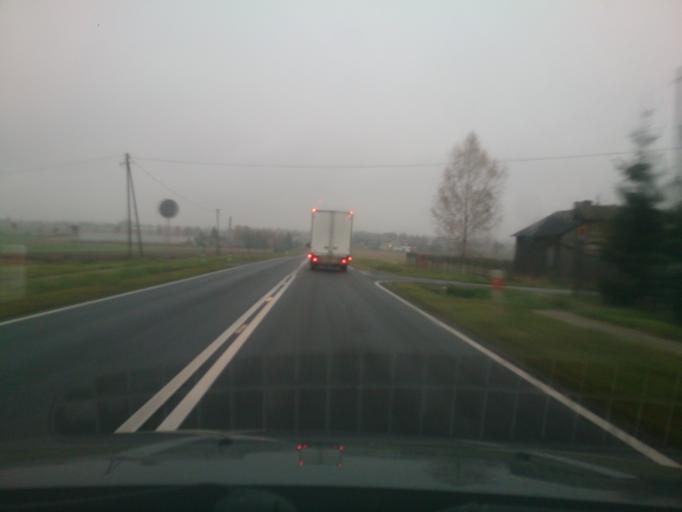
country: PL
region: Greater Poland Voivodeship
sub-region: Powiat kaliski
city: Kozminek
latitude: 51.8592
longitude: 18.2700
